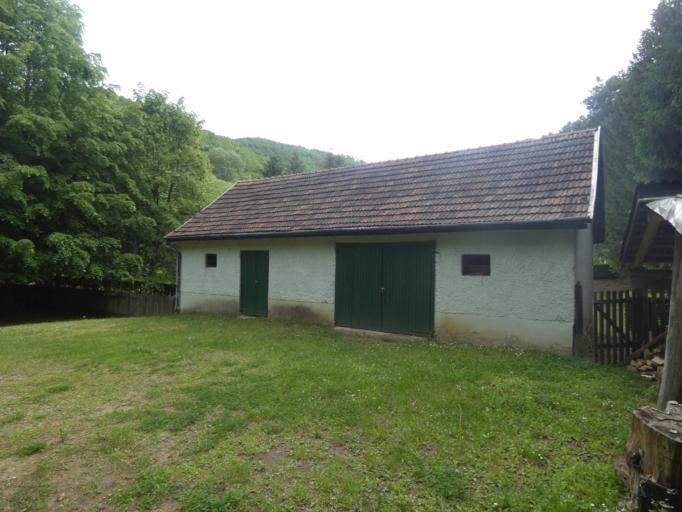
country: HU
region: Heves
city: Petervasara
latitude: 48.1183
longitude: 20.0949
